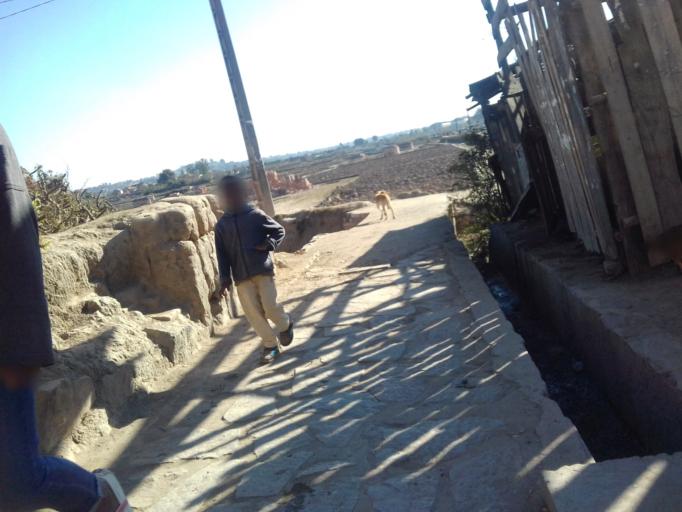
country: MG
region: Analamanga
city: Antananarivo
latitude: -18.8926
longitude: 47.4830
